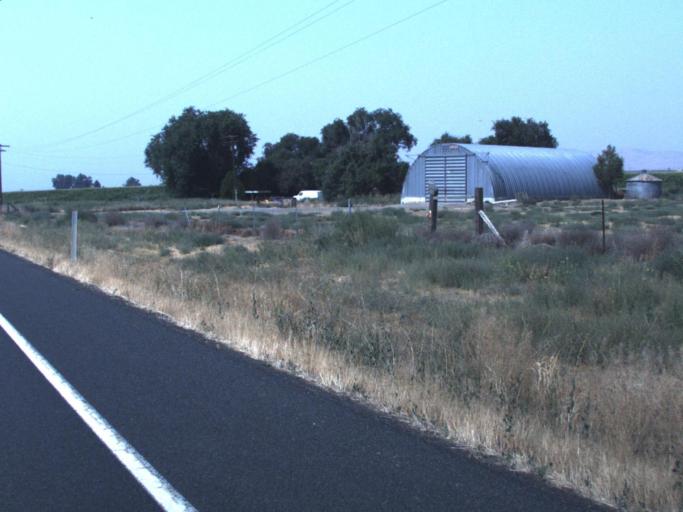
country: US
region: Washington
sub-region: Yakima County
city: Zillah
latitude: 46.5304
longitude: -120.2737
